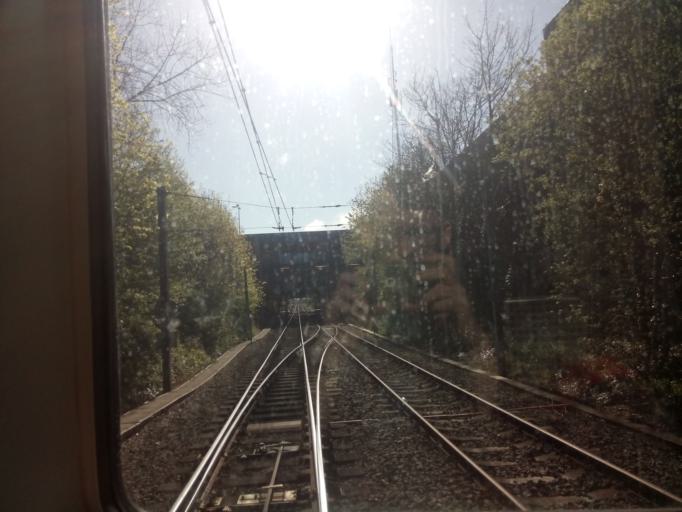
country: GB
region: England
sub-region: Newcastle upon Tyne
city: Gosforth
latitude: 55.0122
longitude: -1.6234
